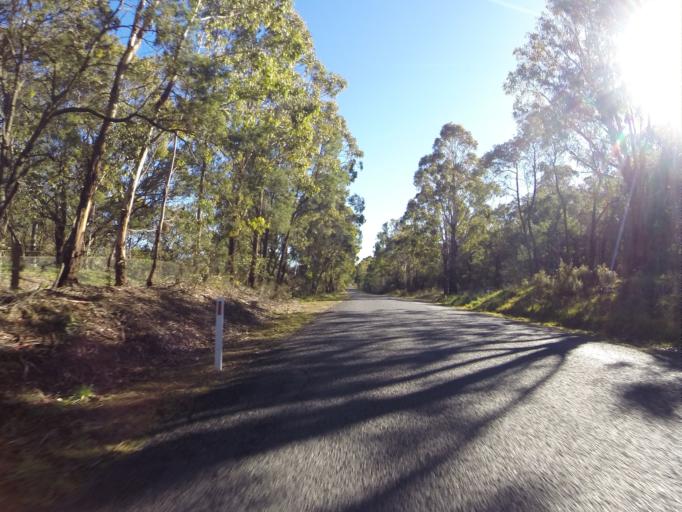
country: AU
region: New South Wales
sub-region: Oberon
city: Oberon
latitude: -33.6616
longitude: 149.8561
